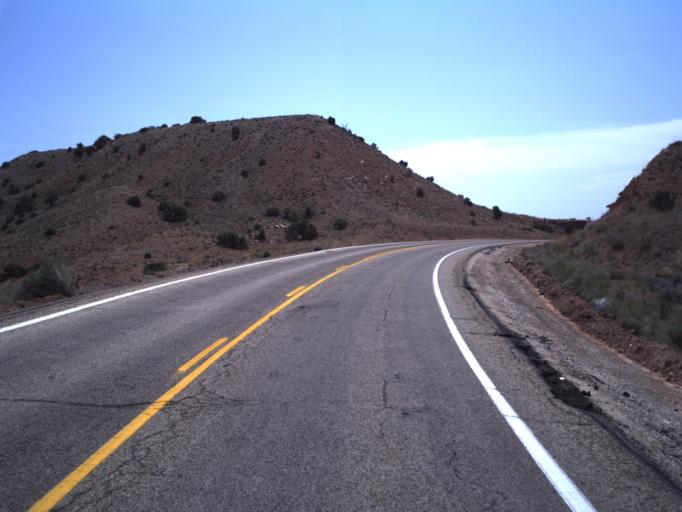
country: US
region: Utah
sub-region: Uintah County
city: Maeser
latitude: 40.4233
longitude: -109.6674
